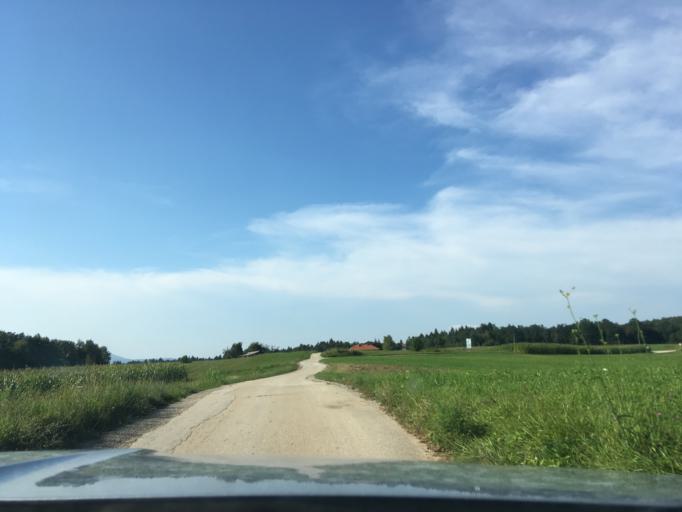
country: SI
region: Crnomelj
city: Crnomelj
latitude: 45.4757
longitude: 15.2083
